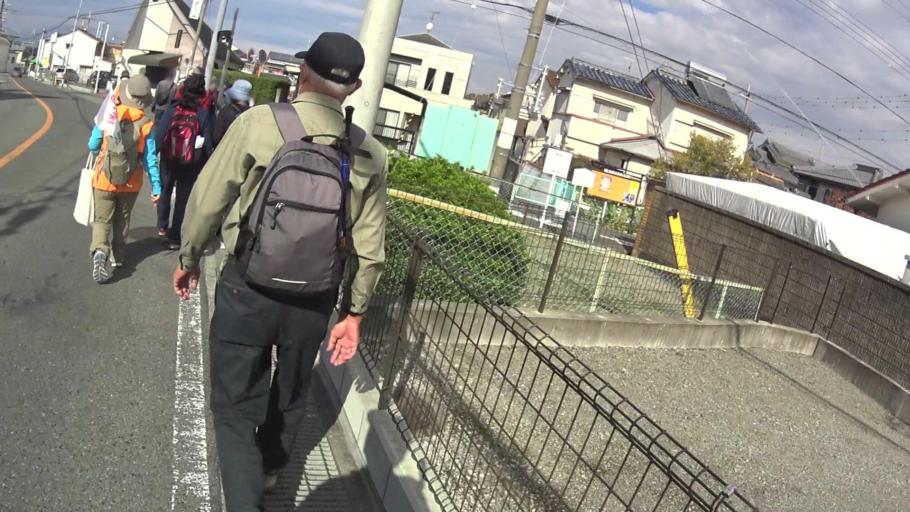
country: JP
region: Osaka
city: Kashihara
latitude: 34.5624
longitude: 135.5923
